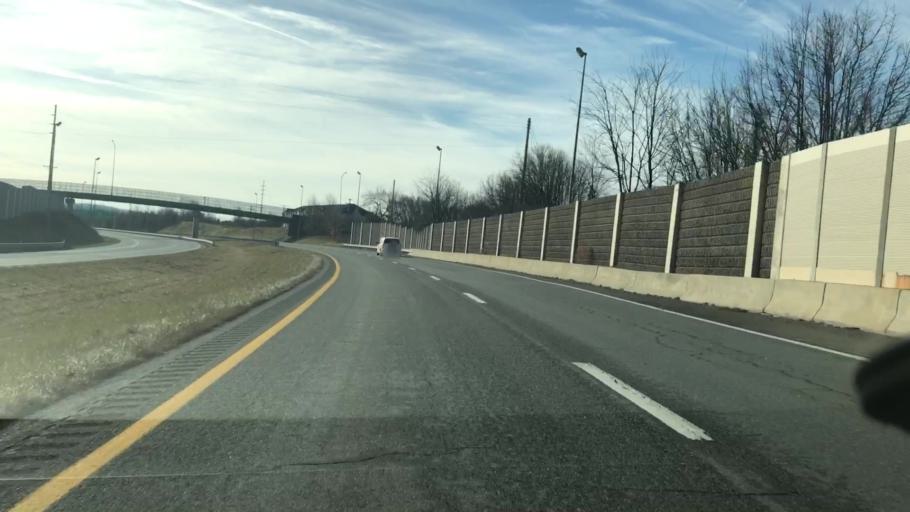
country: US
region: Virginia
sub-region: Montgomery County
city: Merrimac
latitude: 37.1727
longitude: -80.4171
